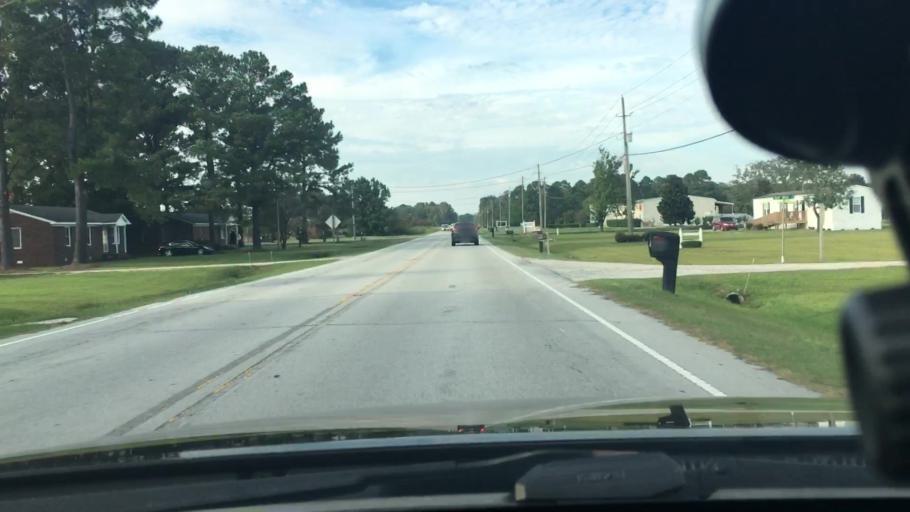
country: US
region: North Carolina
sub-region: Pitt County
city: Windsor
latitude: 35.5165
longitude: -77.3191
